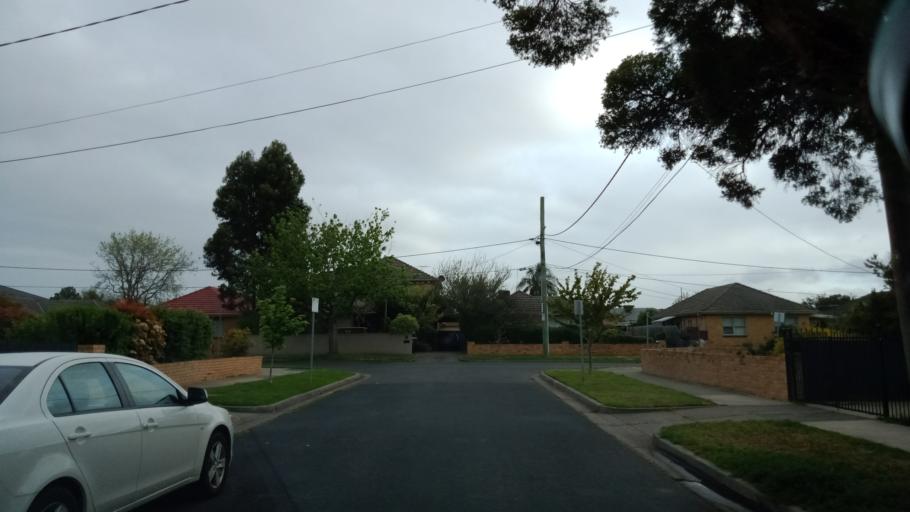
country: AU
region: Victoria
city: McKinnon
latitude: -37.9262
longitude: 145.0622
